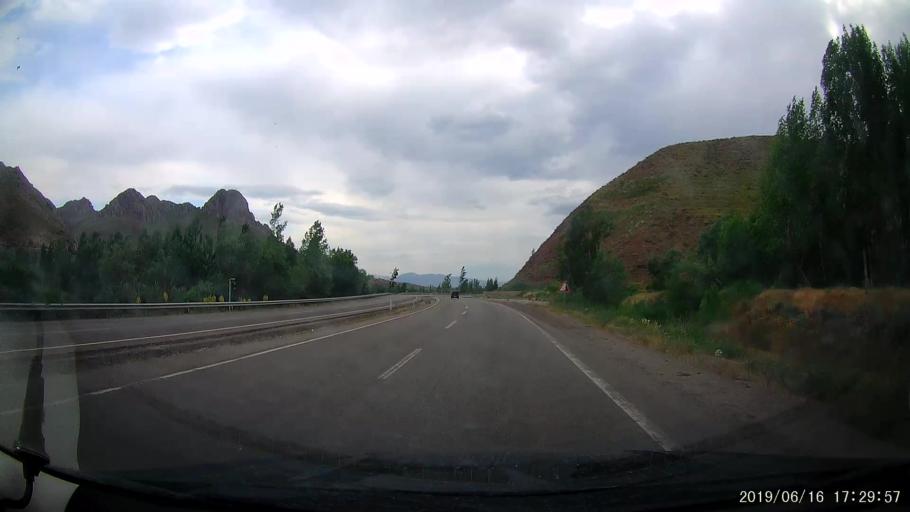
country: TR
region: Erzincan
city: Tercan
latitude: 39.7795
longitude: 40.3566
